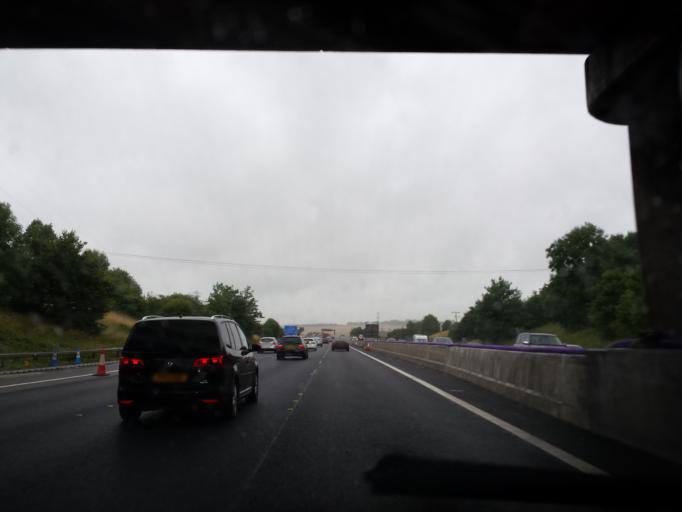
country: GB
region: England
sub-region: Derbyshire
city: Staveley
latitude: 53.2365
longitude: -1.3327
